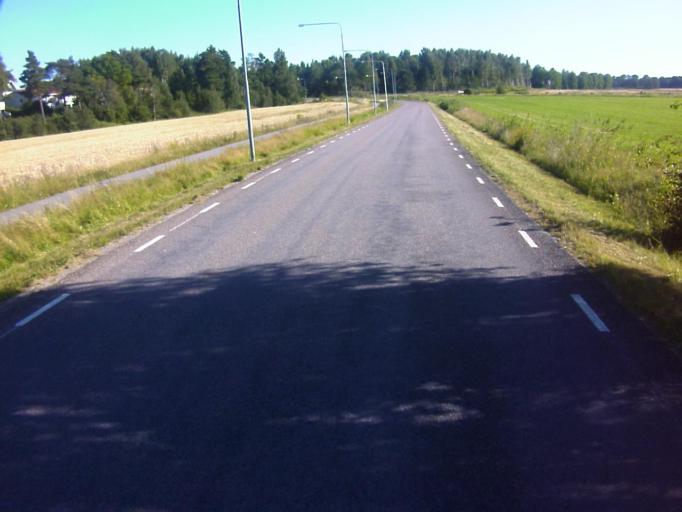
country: SE
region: Soedermanland
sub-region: Eskilstuna Kommun
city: Hallbybrunn
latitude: 59.3846
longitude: 16.4272
